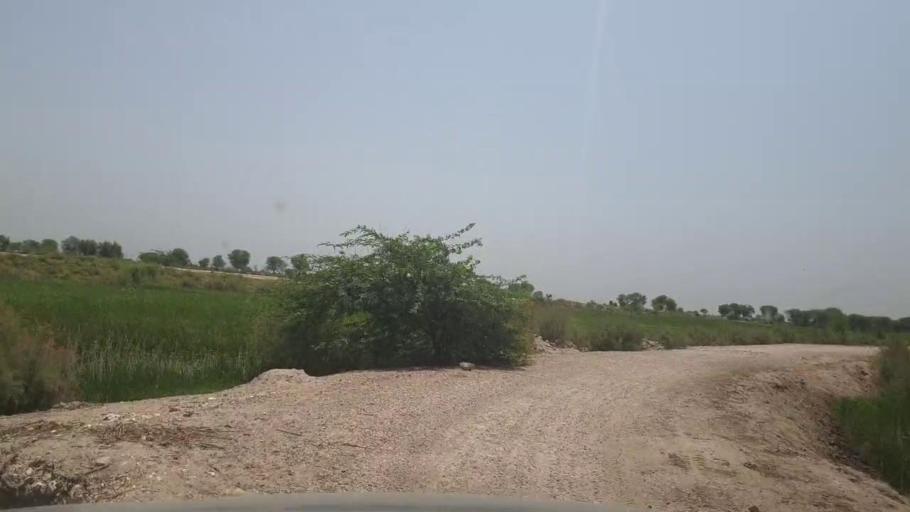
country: PK
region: Sindh
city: Lakhi
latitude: 27.8514
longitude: 68.6651
